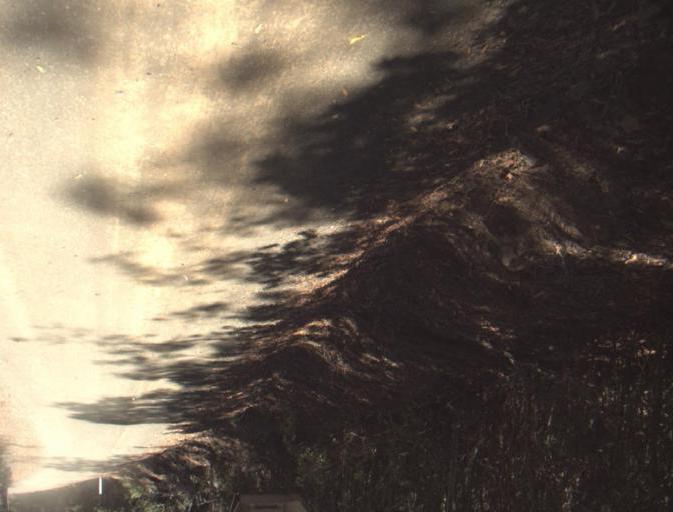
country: AU
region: Tasmania
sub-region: Dorset
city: Scottsdale
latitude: -41.3598
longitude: 147.3964
